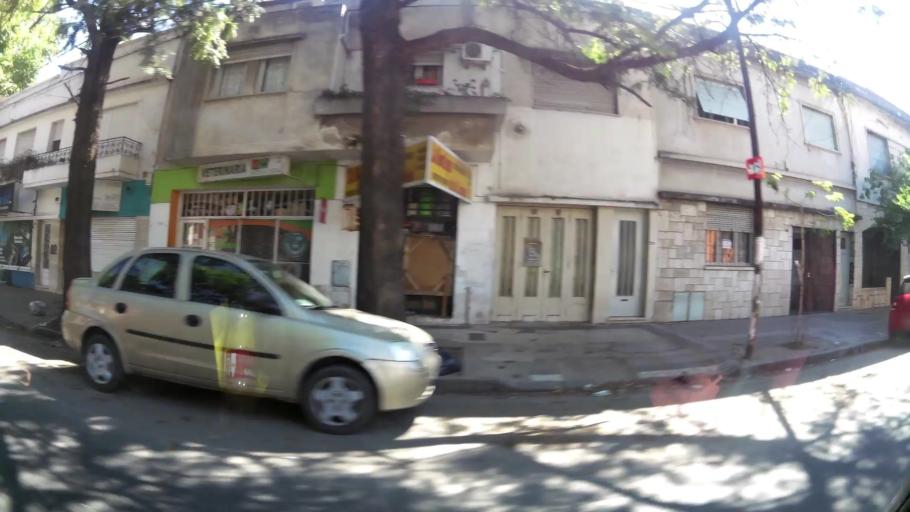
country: AR
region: Cordoba
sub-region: Departamento de Capital
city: Cordoba
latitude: -31.4134
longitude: -64.1714
